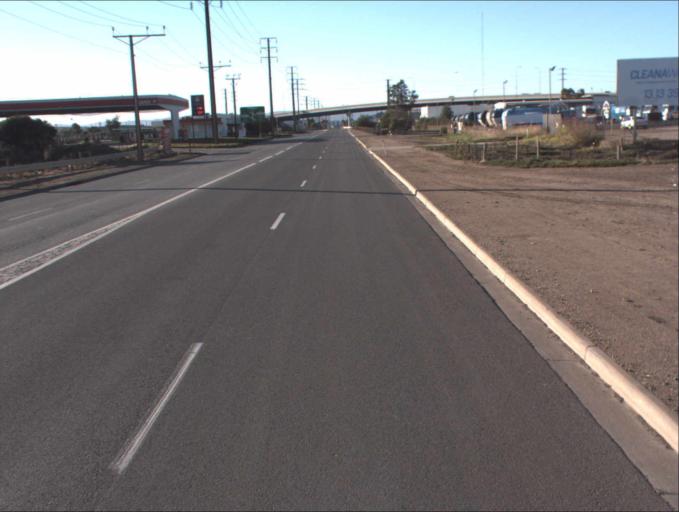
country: AU
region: South Australia
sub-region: Port Adelaide Enfield
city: Birkenhead
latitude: -34.8371
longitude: 138.5186
